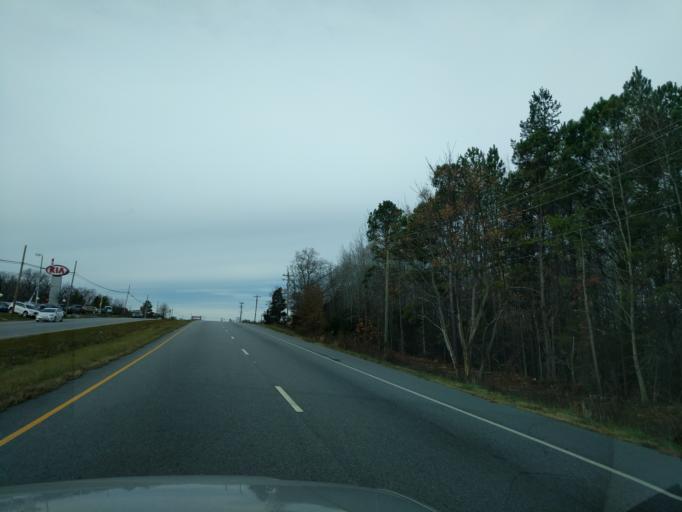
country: US
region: South Carolina
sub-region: Anderson County
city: Northlake
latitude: 34.5831
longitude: -82.7355
